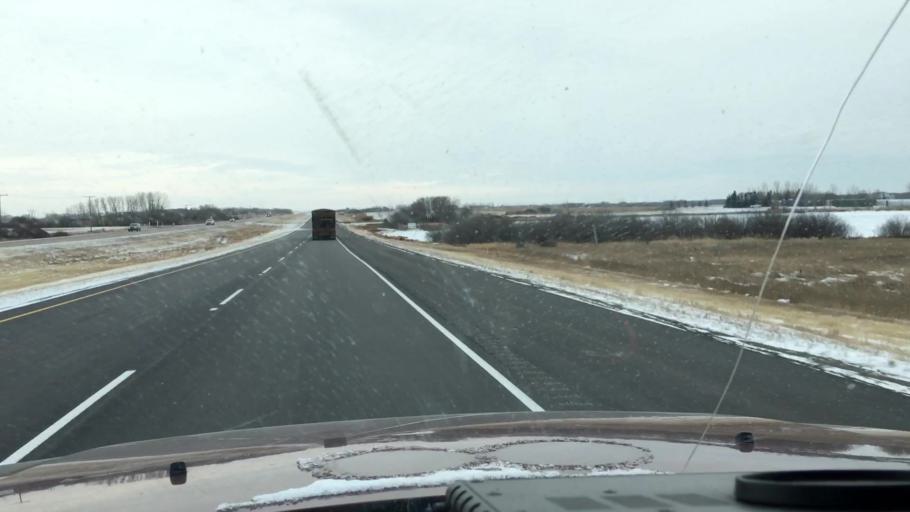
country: CA
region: Saskatchewan
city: Saskatoon
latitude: 51.9242
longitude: -106.5326
